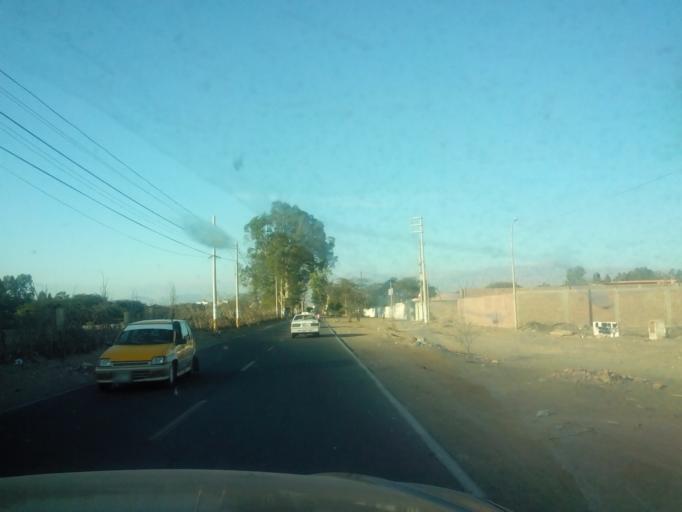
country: PE
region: Ica
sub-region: Provincia de Ica
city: Ica
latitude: -14.0843
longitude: -75.7539
